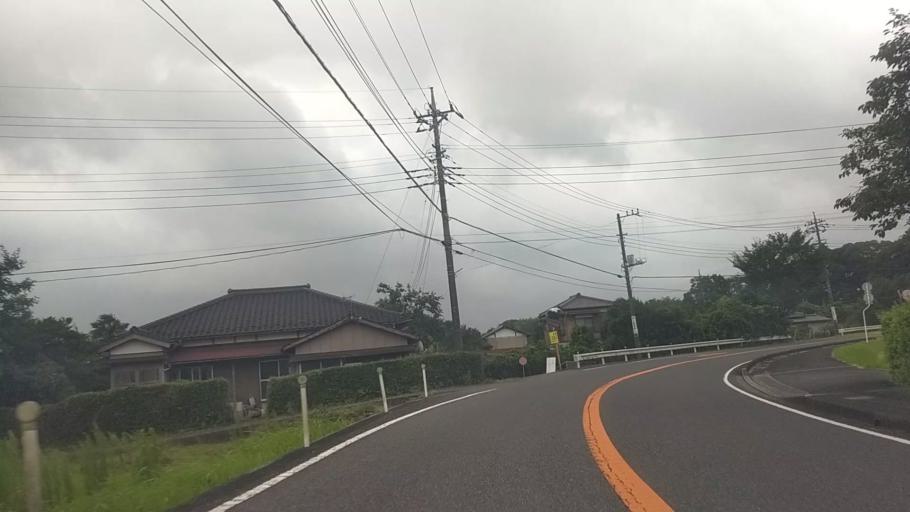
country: JP
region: Chiba
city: Kawaguchi
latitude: 35.2435
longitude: 140.0784
